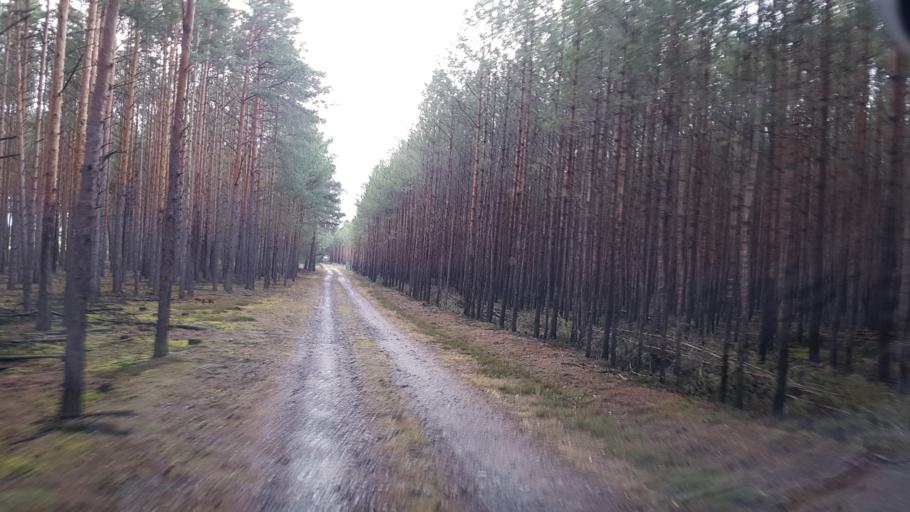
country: DE
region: Brandenburg
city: Sallgast
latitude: 51.6327
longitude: 13.8346
